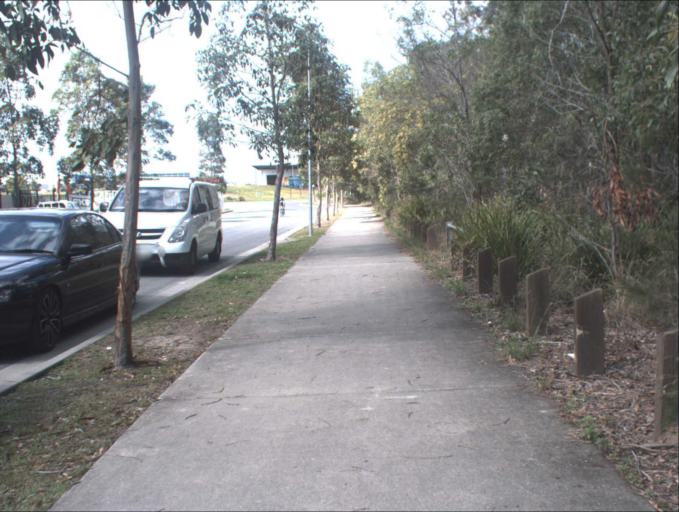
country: AU
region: Queensland
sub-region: Logan
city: Woodridge
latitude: -27.6685
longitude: 153.0758
